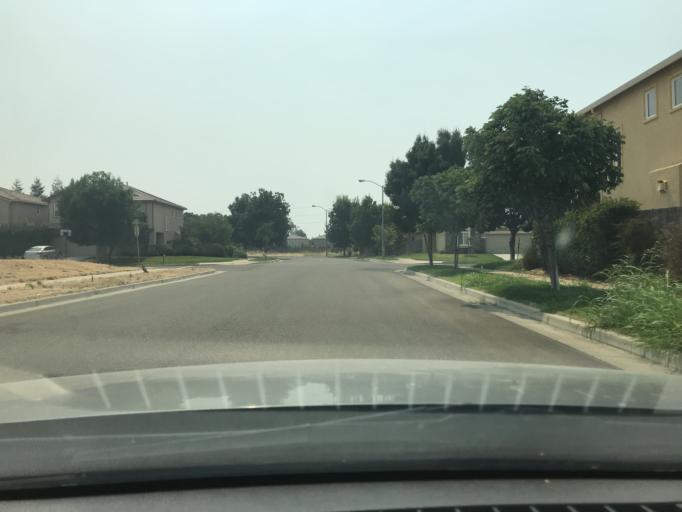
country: US
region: California
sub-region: Merced County
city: Merced
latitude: 37.3436
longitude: -120.4830
